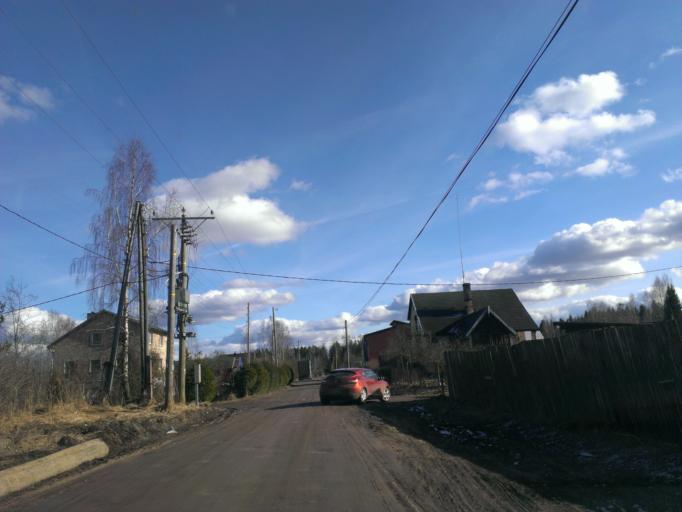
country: LV
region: Garkalne
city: Garkalne
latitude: 56.9497
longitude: 24.4489
